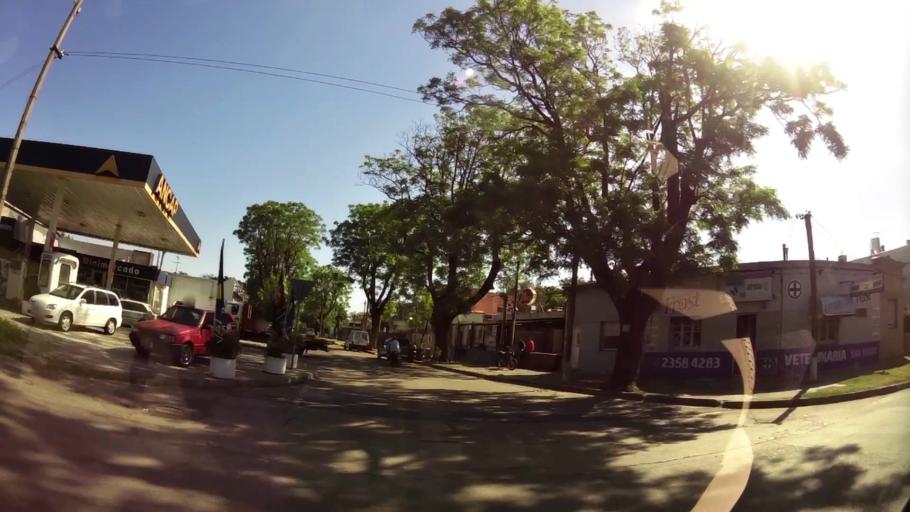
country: UY
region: Montevideo
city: Montevideo
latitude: -34.8349
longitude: -56.2144
